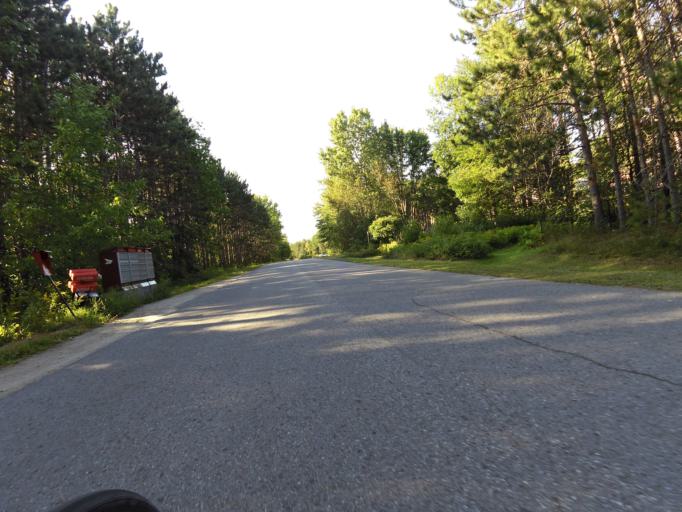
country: CA
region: Ontario
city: Bells Corners
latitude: 45.4683
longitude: -76.0325
